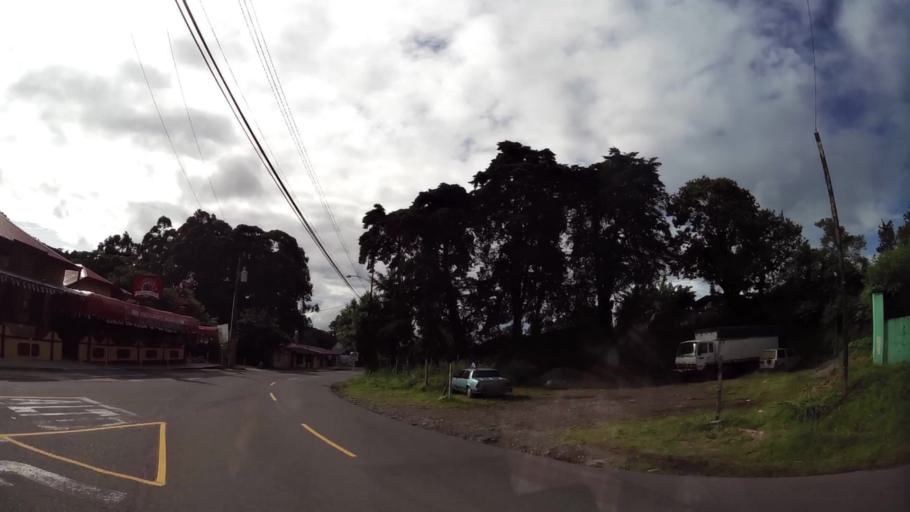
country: PA
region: Chiriqui
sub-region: Distrito Boquete
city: Boquete
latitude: 8.7815
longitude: -82.4324
